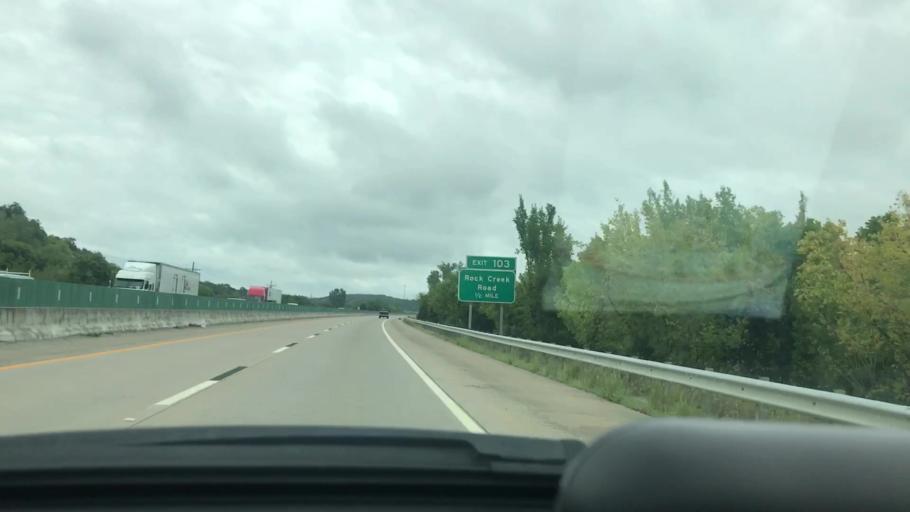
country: US
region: Oklahoma
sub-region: Pittsburg County
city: Krebs
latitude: 35.0919
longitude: -95.7000
